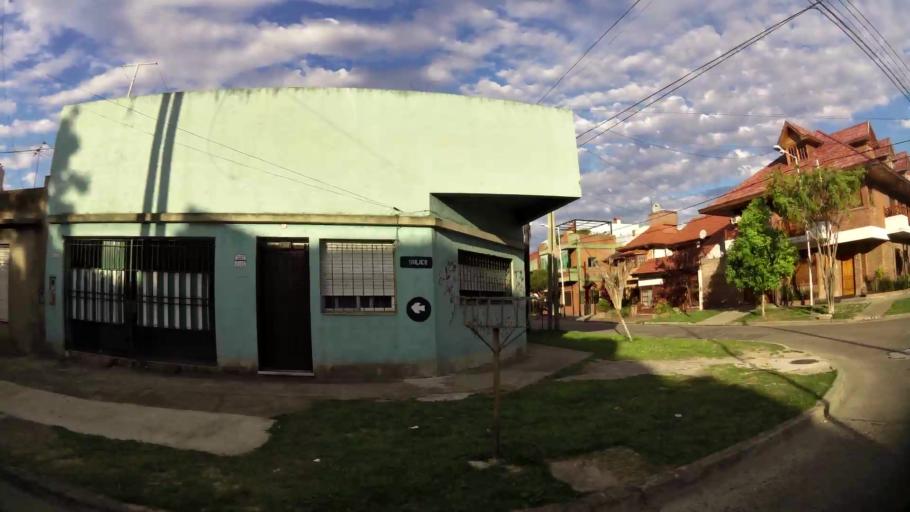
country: AR
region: Buenos Aires
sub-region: Partido de Avellaneda
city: Avellaneda
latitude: -34.6875
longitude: -58.3471
